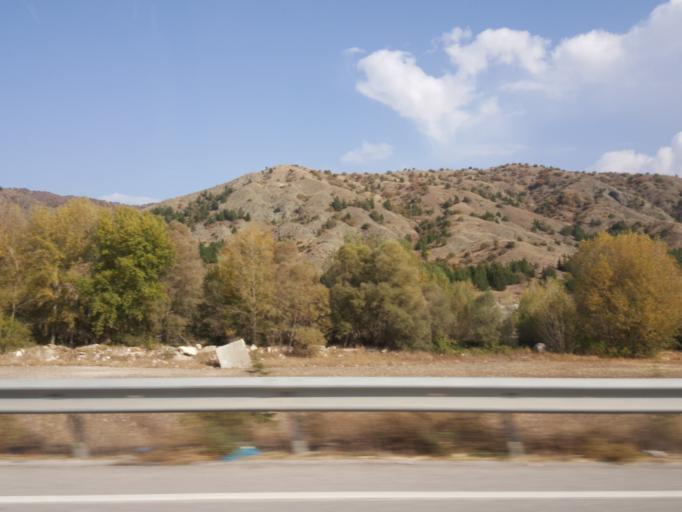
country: TR
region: Corum
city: Seydim
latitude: 40.3653
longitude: 34.7307
